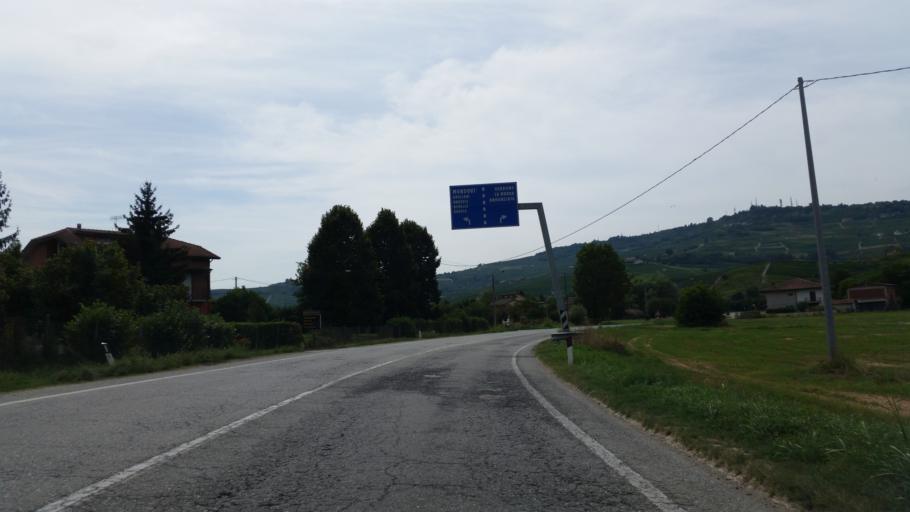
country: IT
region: Piedmont
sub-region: Provincia di Cuneo
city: Castiglione Falletto
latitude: 44.6319
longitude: 7.9651
